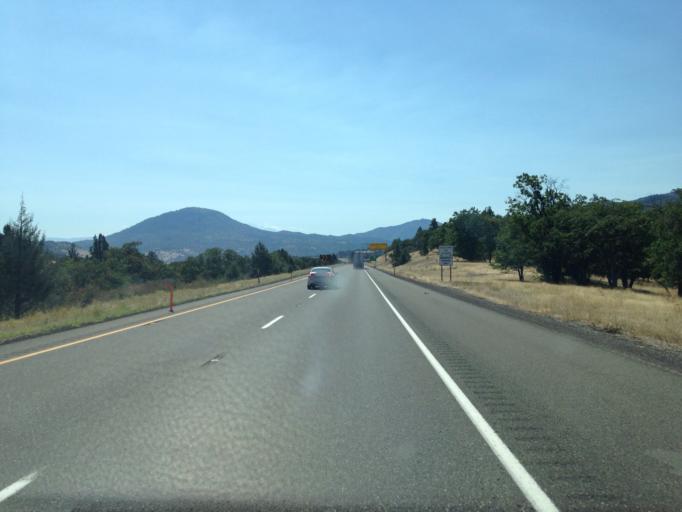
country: US
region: California
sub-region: Siskiyou County
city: Yreka
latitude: 41.9428
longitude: -122.5870
